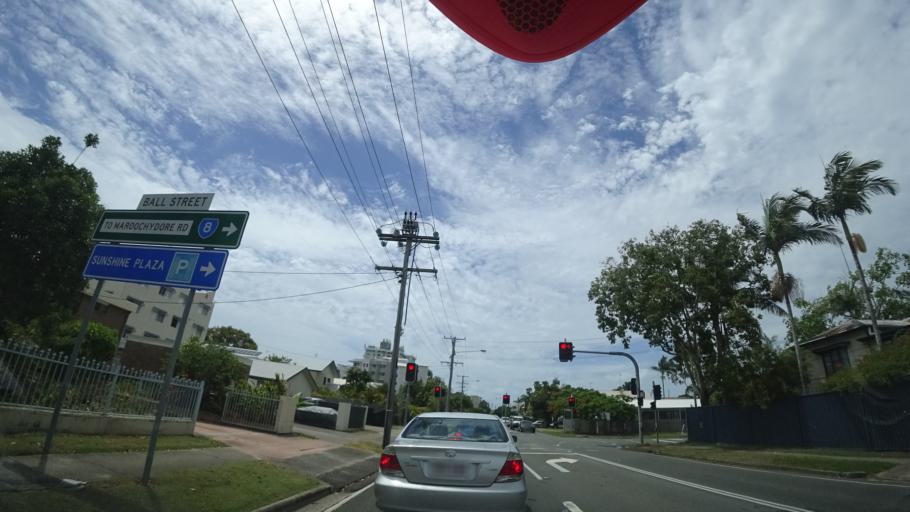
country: AU
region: Queensland
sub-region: Sunshine Coast
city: Buderim
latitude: -26.6459
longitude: 153.0860
